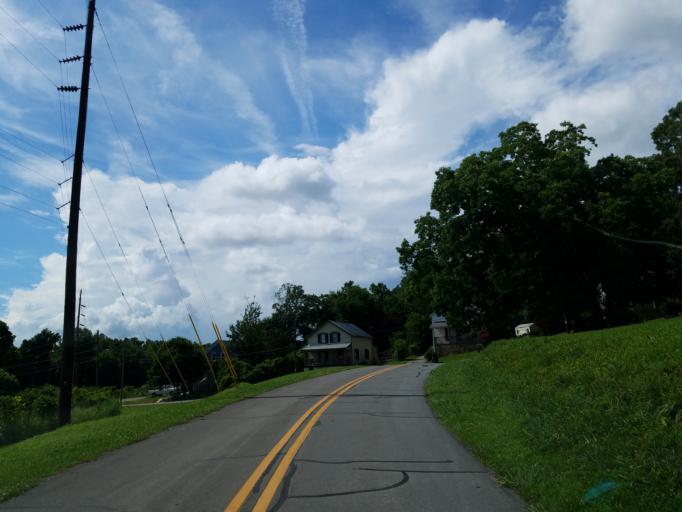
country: US
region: Georgia
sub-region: Pickens County
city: Nelson
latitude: 34.3837
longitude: -84.3706
